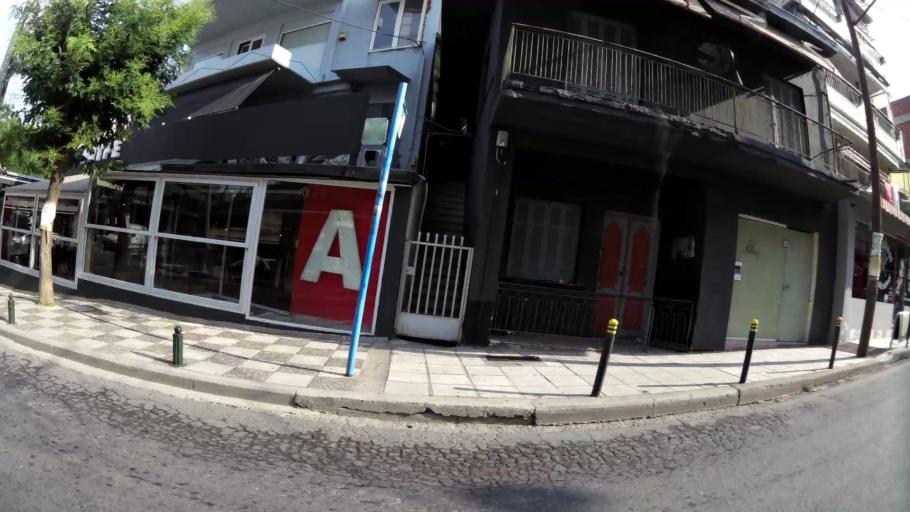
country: GR
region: Central Macedonia
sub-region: Nomos Thessalonikis
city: Polichni
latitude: 40.6584
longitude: 22.9434
